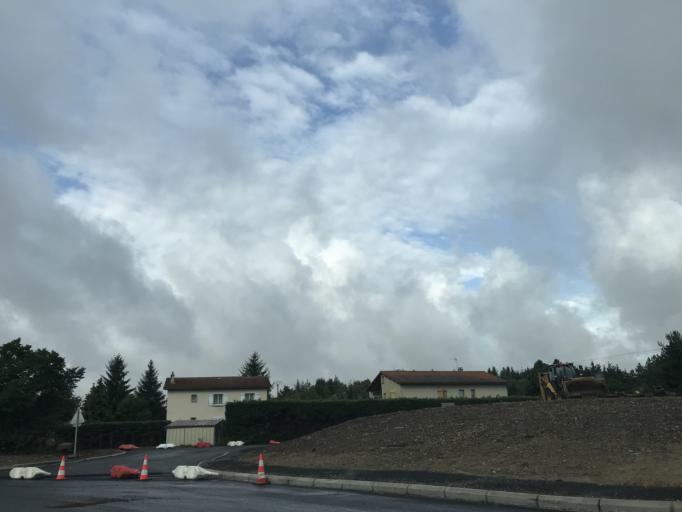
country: FR
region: Auvergne
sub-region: Departement de la Haute-Loire
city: Saint-Paulien
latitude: 45.1034
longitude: 3.8114
